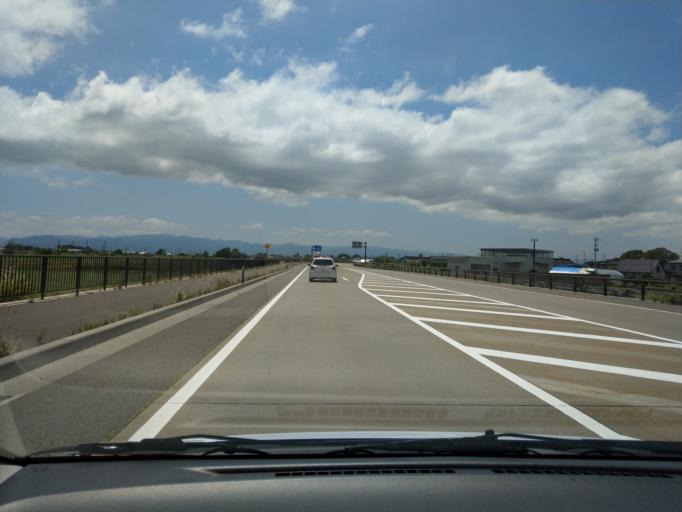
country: JP
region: Aomori
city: Namioka
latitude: 40.6940
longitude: 140.5634
